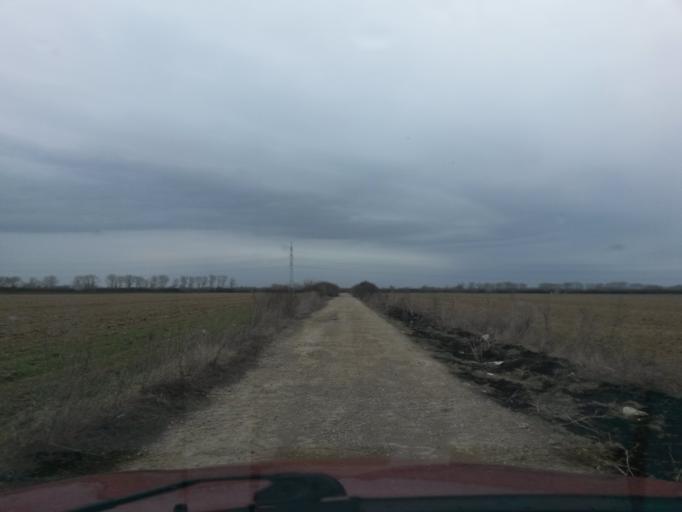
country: SK
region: Kosicky
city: Michalovce
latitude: 48.6916
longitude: 21.8902
